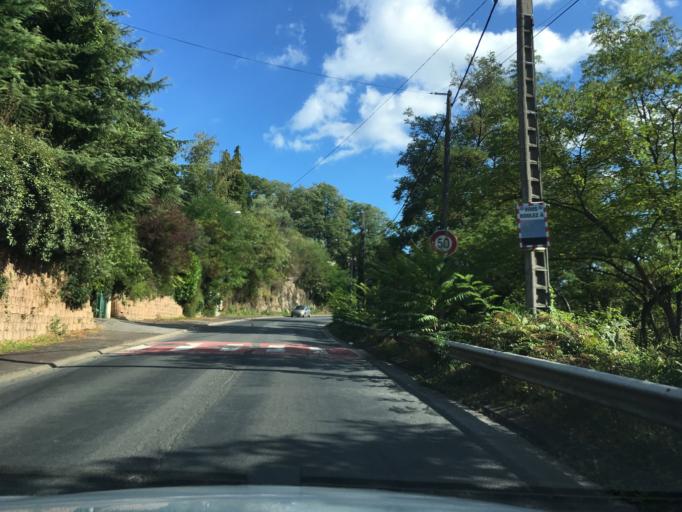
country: FR
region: Limousin
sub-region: Departement de la Correze
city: Brive-la-Gaillarde
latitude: 45.1463
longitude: 1.5463
